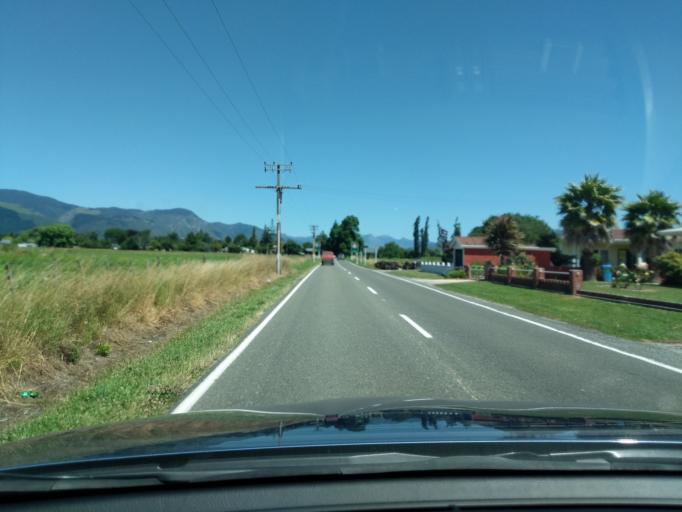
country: NZ
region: Tasman
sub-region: Tasman District
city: Takaka
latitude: -40.8414
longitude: 172.8016
